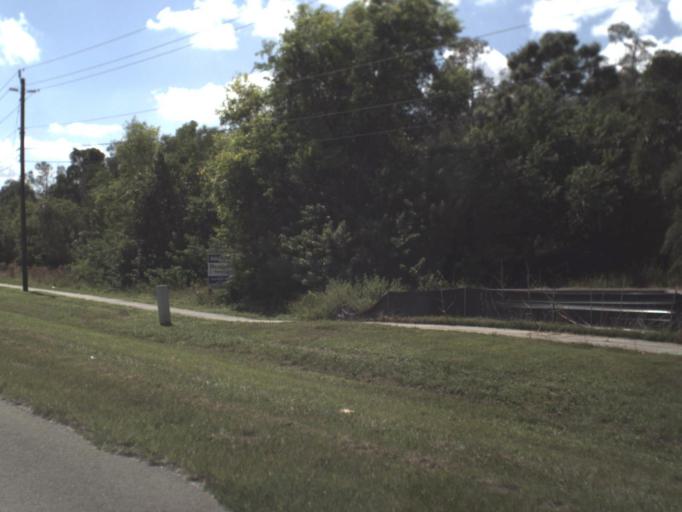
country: US
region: Florida
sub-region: Lee County
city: San Carlos Park
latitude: 26.4897
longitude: -81.8435
